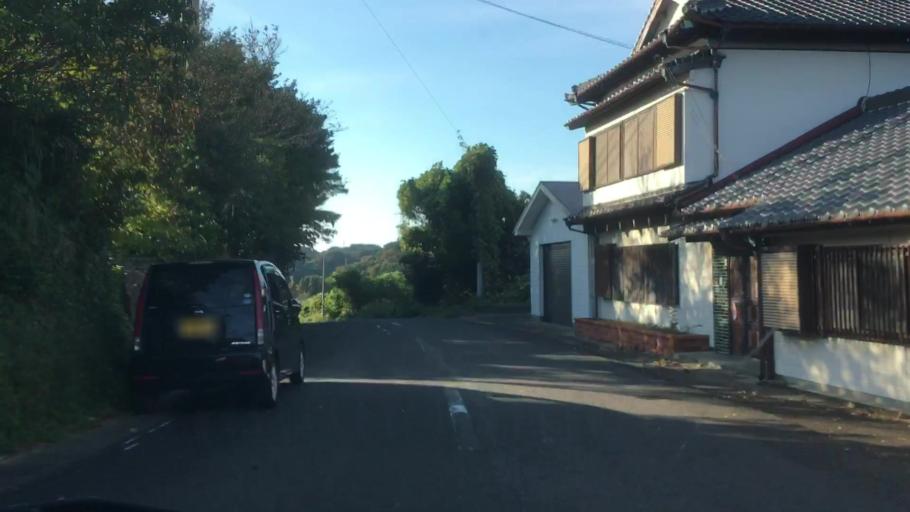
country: JP
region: Nagasaki
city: Sasebo
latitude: 33.0213
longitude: 129.5736
